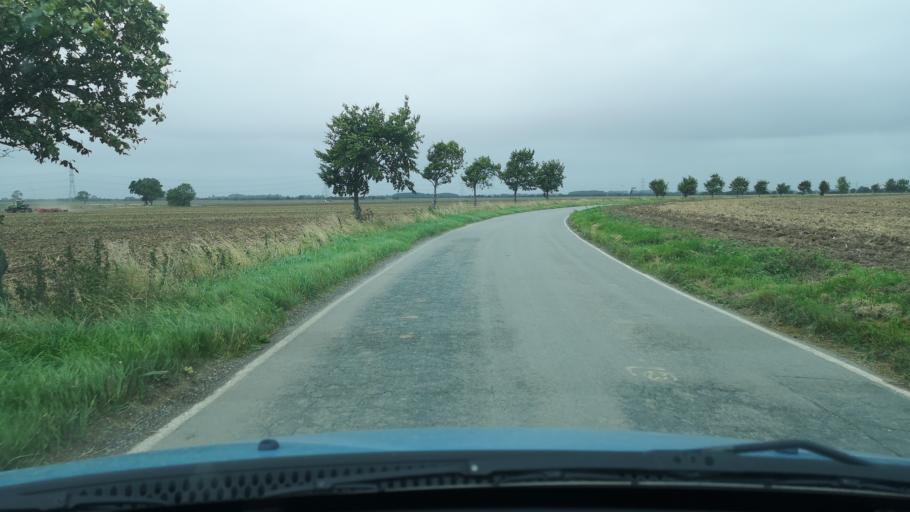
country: GB
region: England
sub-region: North Lincolnshire
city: Burton upon Stather
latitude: 53.6676
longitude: -0.7199
